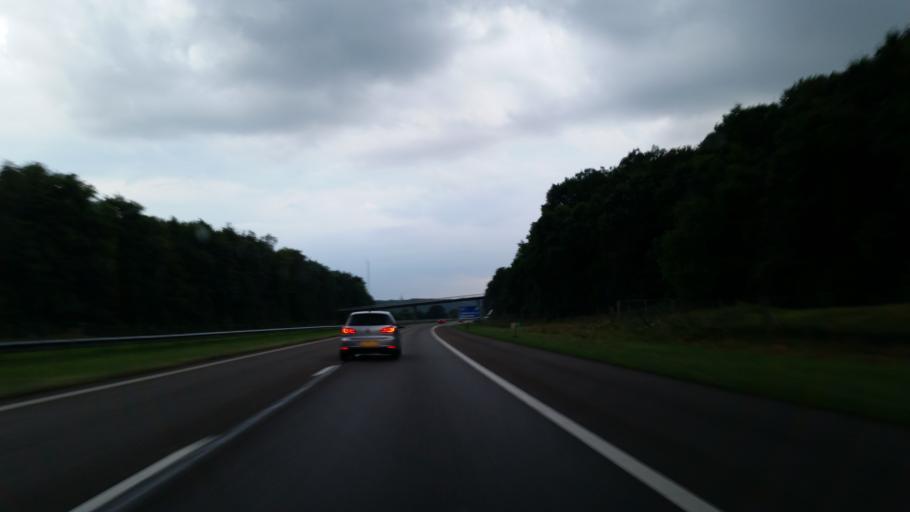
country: NL
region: Limburg
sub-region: Valkenburg aan de Geul
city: Broekhem
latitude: 50.8770
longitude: 5.8270
